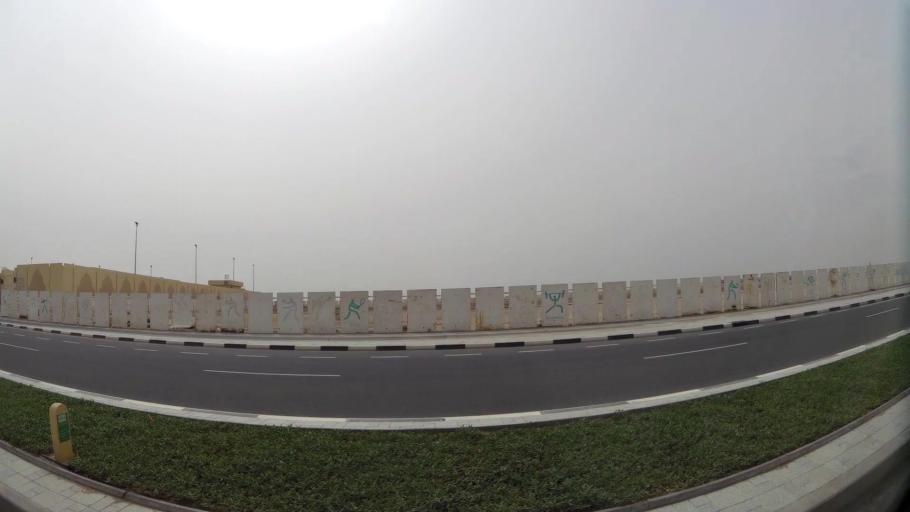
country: QA
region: Baladiyat ad Dawhah
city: Doha
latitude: 25.2251
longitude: 51.5362
